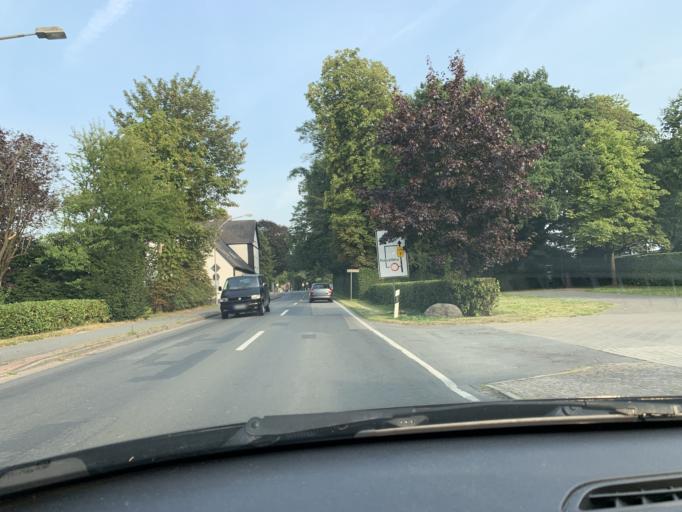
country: DE
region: Lower Saxony
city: Barssel
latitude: 53.1764
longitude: 7.7652
